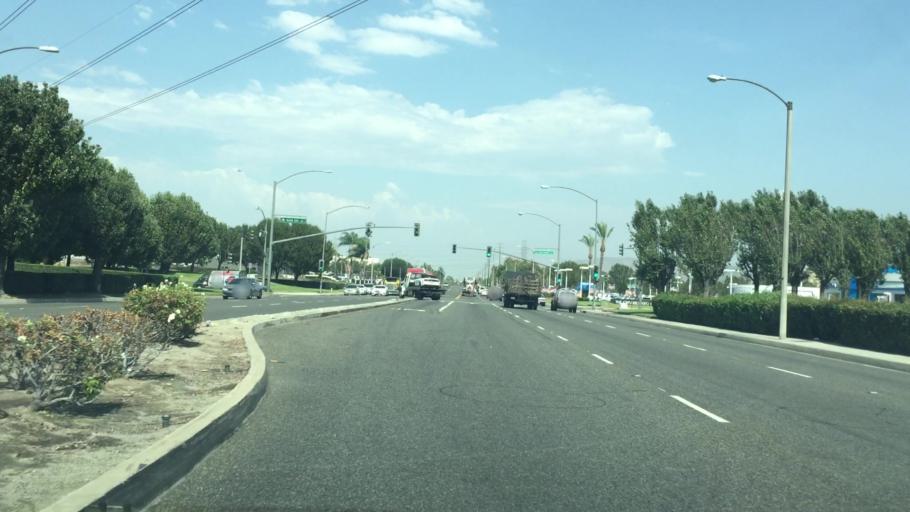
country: US
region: California
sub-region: Riverside County
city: Mira Loma
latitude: 34.0481
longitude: -117.5461
